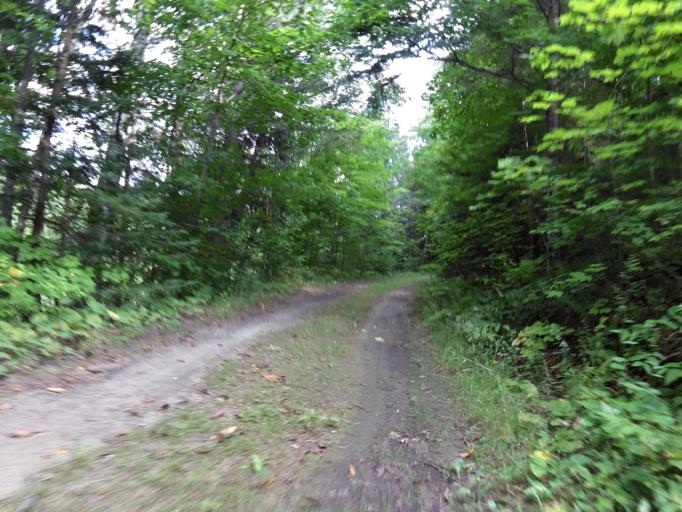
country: CA
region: Quebec
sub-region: Outaouais
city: Wakefield
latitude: 45.6438
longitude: -75.9992
